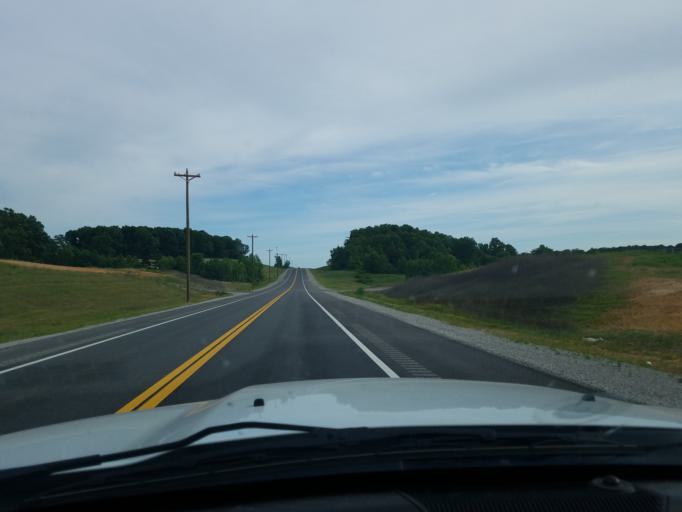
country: US
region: Tennessee
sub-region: Putnam County
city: Cookeville
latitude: 36.1688
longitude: -85.5621
